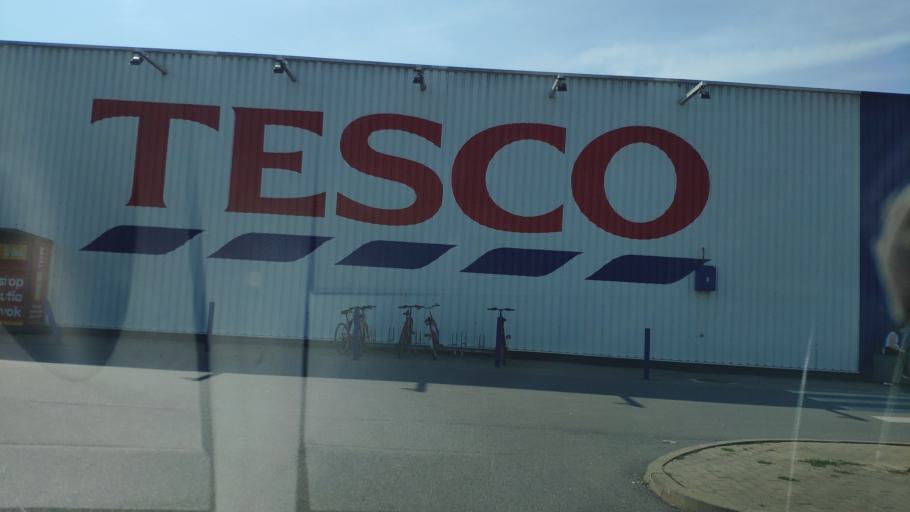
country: SK
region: Presovsky
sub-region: Okres Presov
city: Presov
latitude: 49.0091
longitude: 21.2203
